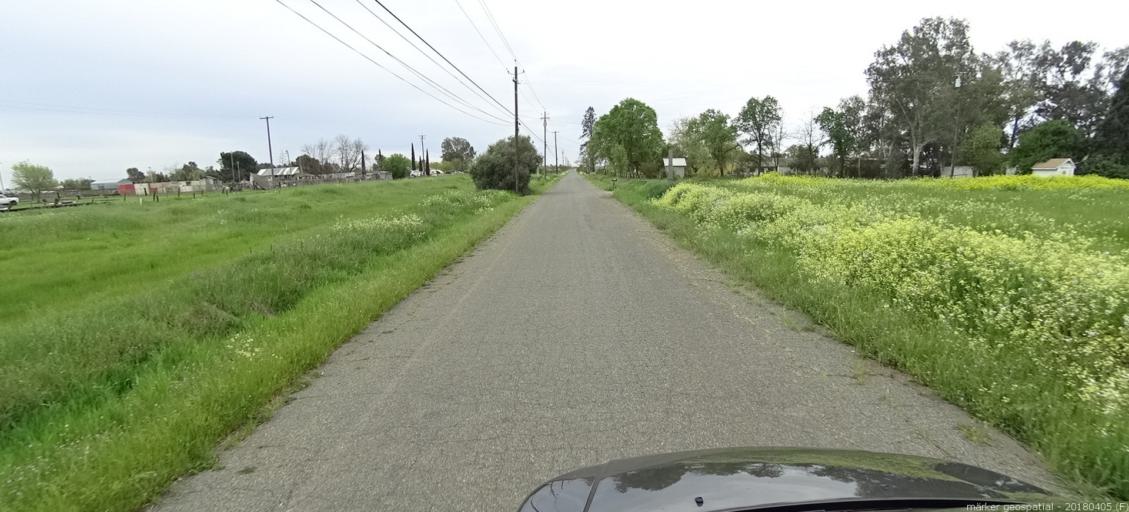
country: US
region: California
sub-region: Sacramento County
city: Herald
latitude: 38.2849
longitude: -121.2450
